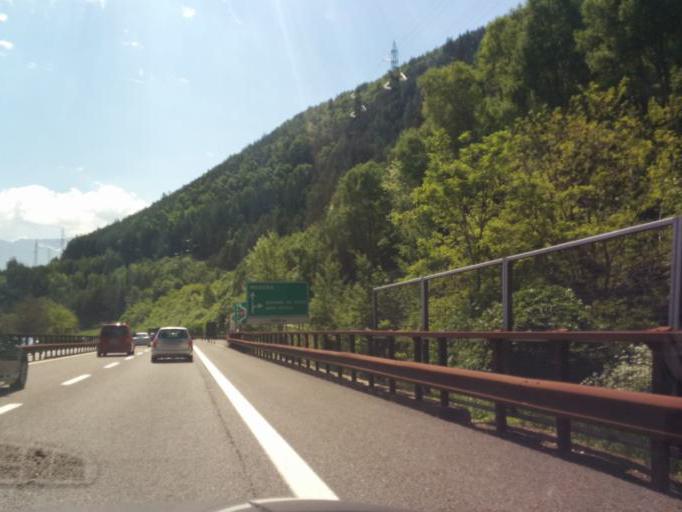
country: IT
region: Trentino-Alto Adige
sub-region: Bolzano
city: Fortezza
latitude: 46.7761
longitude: 11.6278
